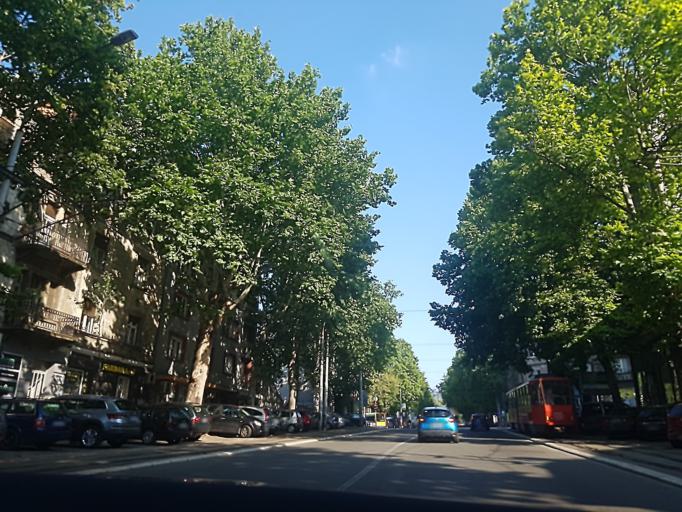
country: RS
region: Central Serbia
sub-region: Belgrade
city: Stari Grad
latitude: 44.8173
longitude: 20.4682
